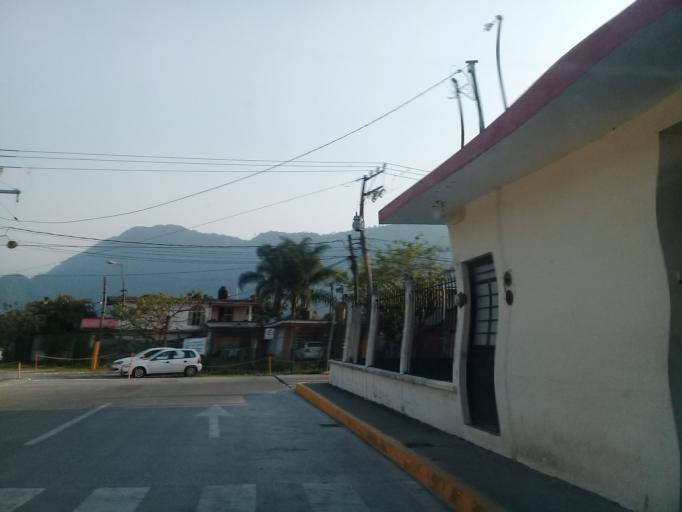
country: MX
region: Veracruz
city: Ixtac Zoquitlan
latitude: 18.8521
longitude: -97.0530
